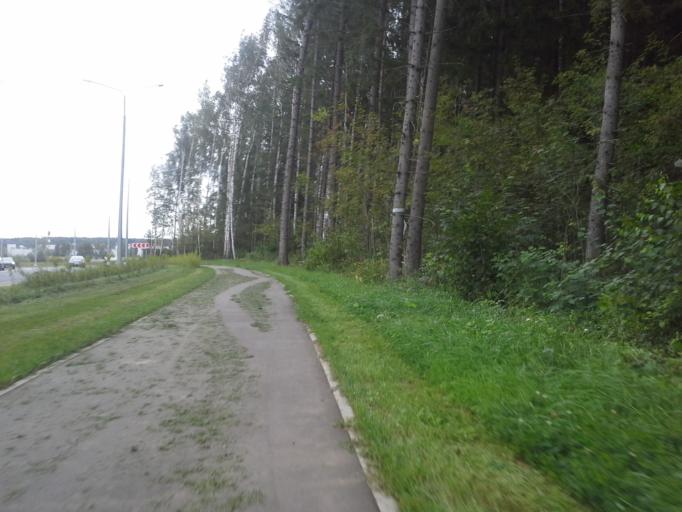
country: RU
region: Moskovskaya
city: Kokoshkino
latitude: 55.5764
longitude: 37.1651
